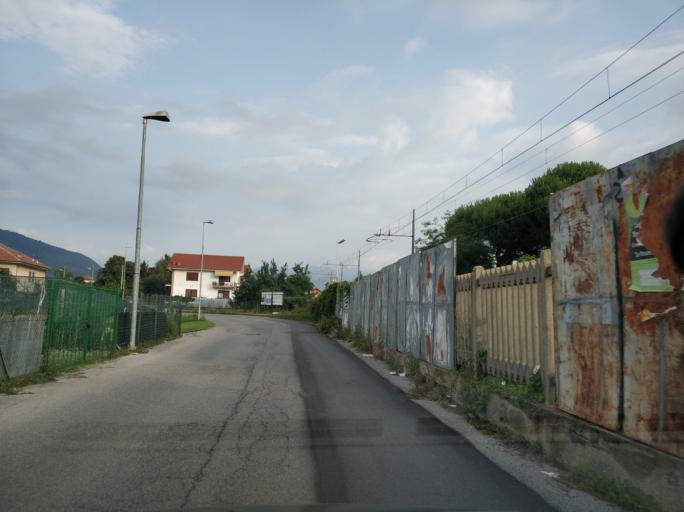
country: IT
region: Piedmont
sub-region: Provincia di Torino
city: Mathi
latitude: 45.2537
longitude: 7.5447
